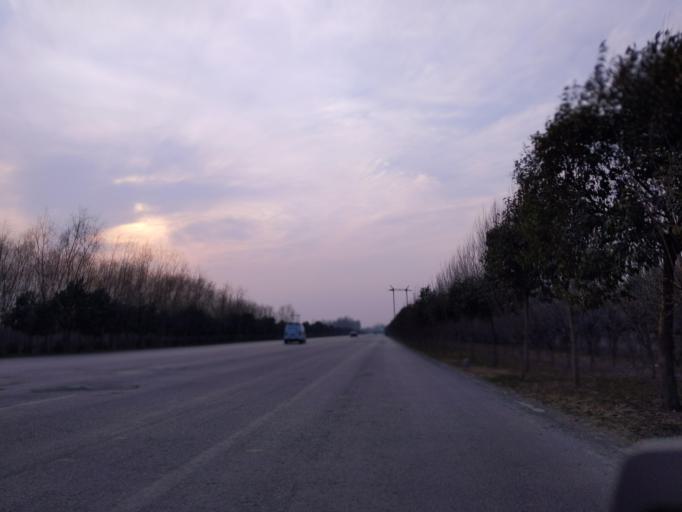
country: CN
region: Henan Sheng
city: Puyang
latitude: 35.8196
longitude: 114.9890
